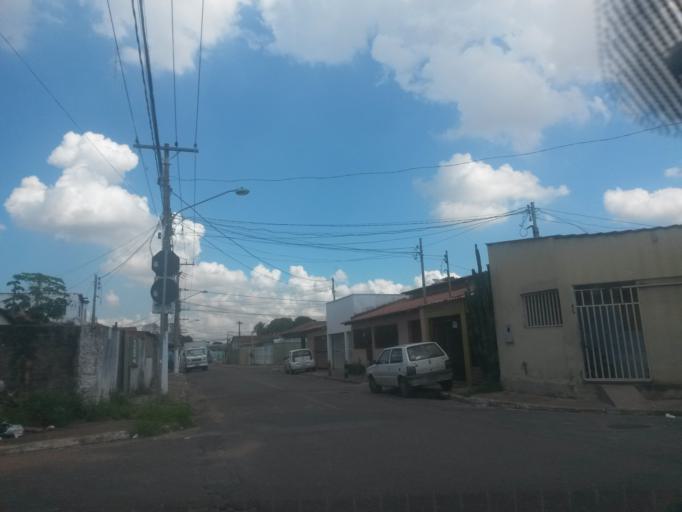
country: BR
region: Mato Grosso
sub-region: Cuiaba
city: Cuiaba
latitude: -15.5997
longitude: -56.0803
